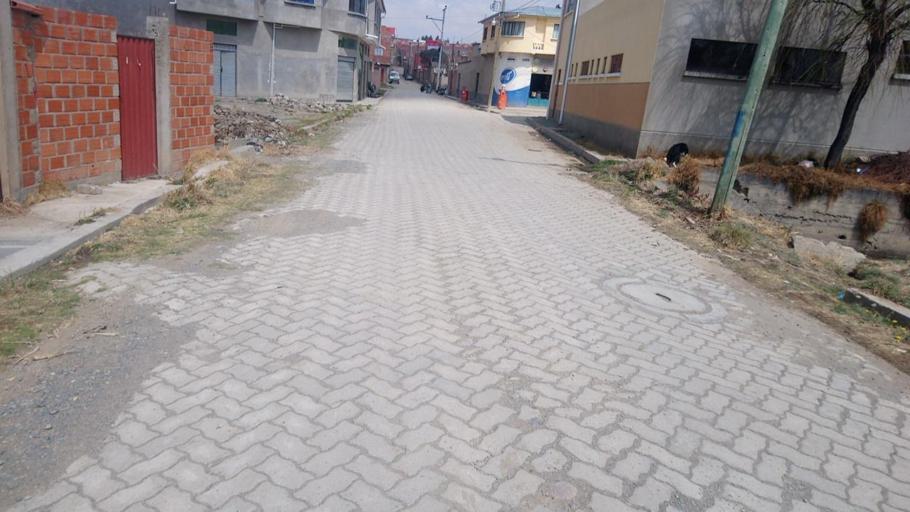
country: BO
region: La Paz
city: Batallas
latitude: -16.3999
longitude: -68.4753
